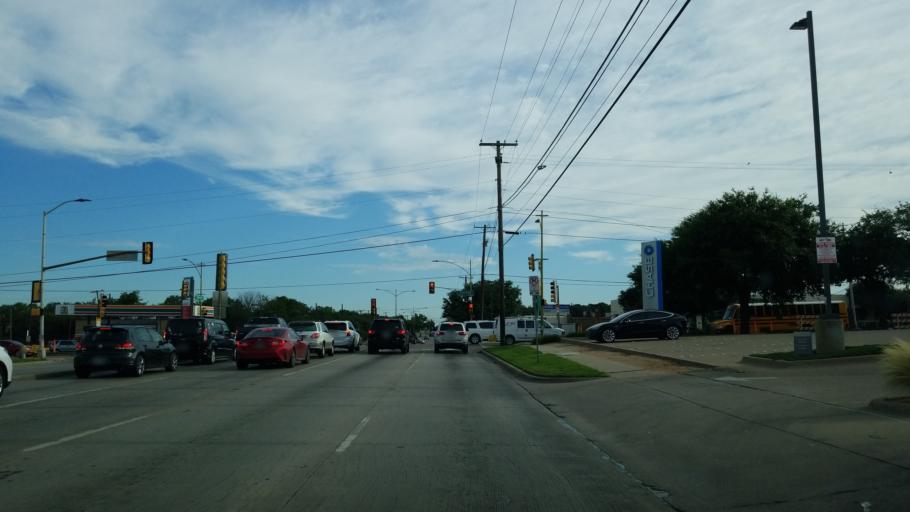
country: US
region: Texas
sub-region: Dallas County
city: Farmers Branch
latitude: 32.9090
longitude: -96.8560
